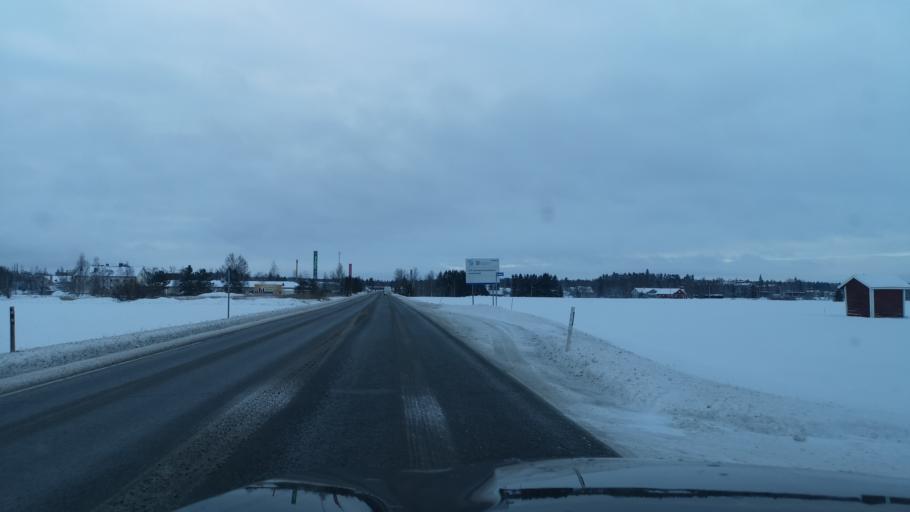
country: FI
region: Varsinais-Suomi
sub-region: Loimaa
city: Loimaa
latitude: 60.8618
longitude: 23.0482
